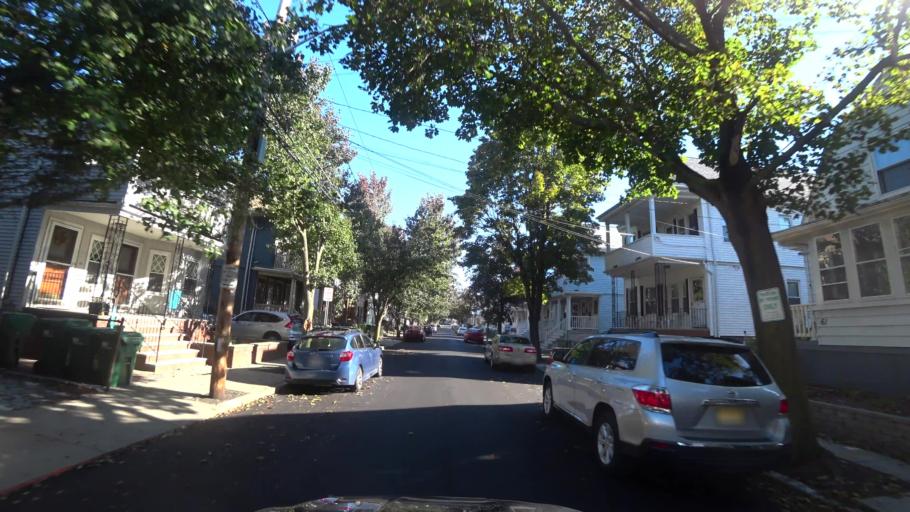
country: US
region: Massachusetts
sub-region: Middlesex County
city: Medford
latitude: 42.4022
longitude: -71.1142
